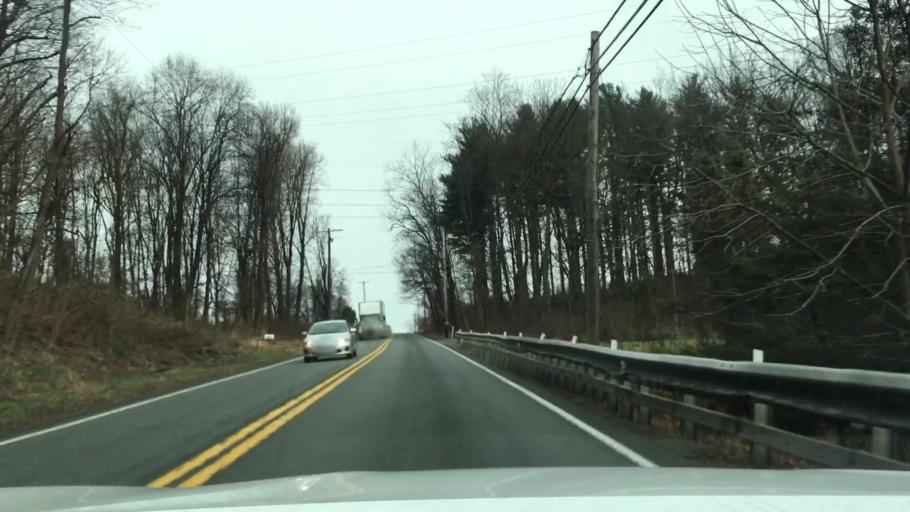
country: US
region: Pennsylvania
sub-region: Lehigh County
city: Macungie
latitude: 40.4711
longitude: -75.5386
